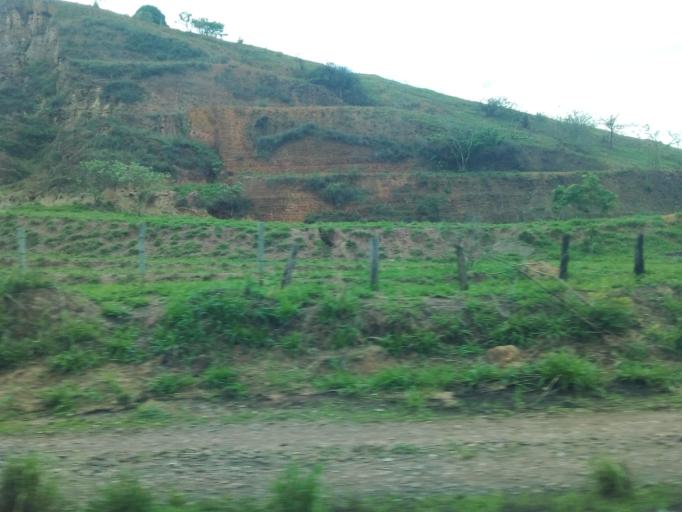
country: BR
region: Minas Gerais
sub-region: Governador Valadares
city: Governador Valadares
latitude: -19.0704
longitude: -42.1513
